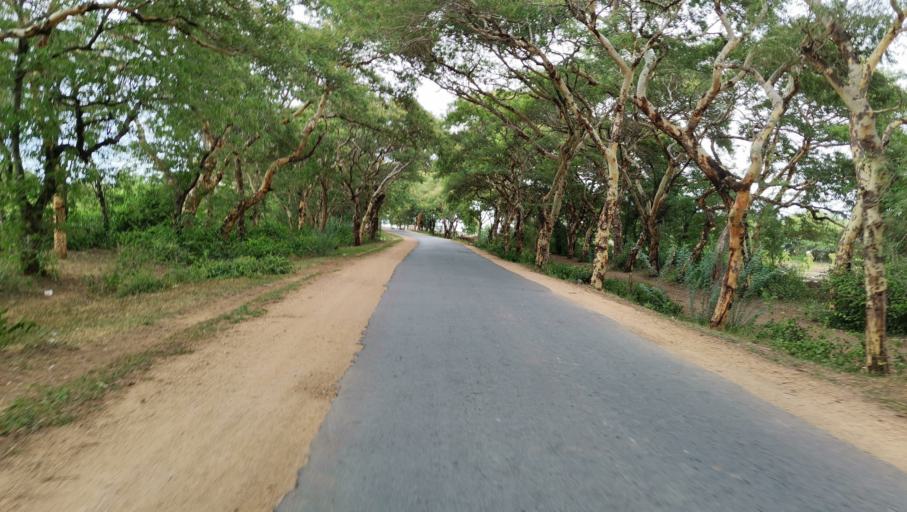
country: MM
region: Sagain
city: Monywa
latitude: 21.8544
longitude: 95.4383
